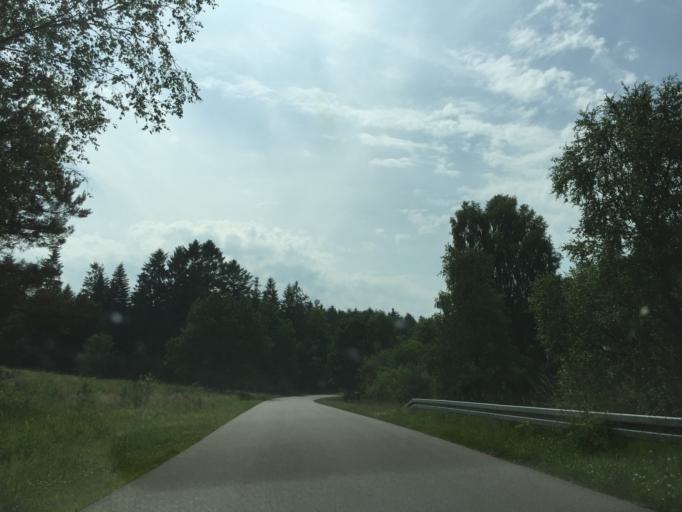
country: DK
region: Central Jutland
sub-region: Silkeborg Kommune
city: Virklund
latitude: 56.0549
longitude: 9.4572
